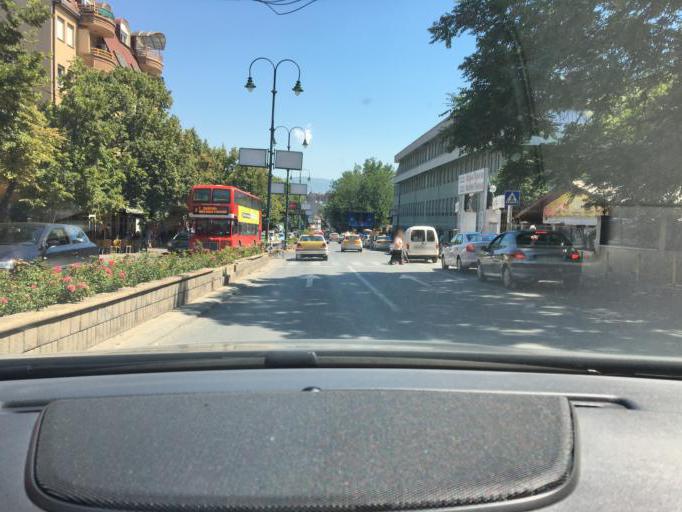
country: MK
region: Karpos
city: Skopje
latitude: 41.9895
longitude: 21.4195
